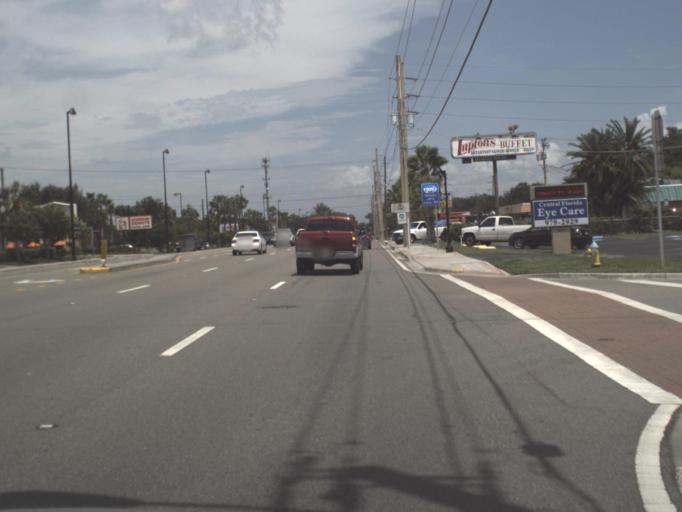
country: US
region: Florida
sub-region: Hillsborough County
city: Temple Terrace
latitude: 28.0325
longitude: -82.3983
